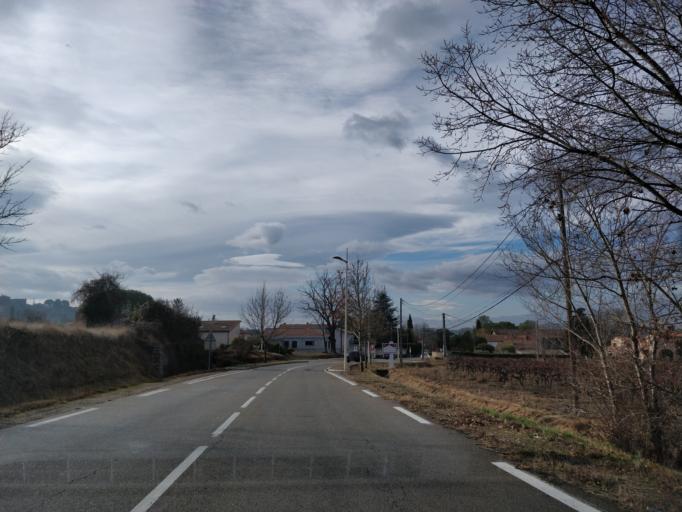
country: FR
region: Languedoc-Roussillon
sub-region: Departement du Gard
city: Villevieille
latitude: 43.7961
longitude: 4.0966
